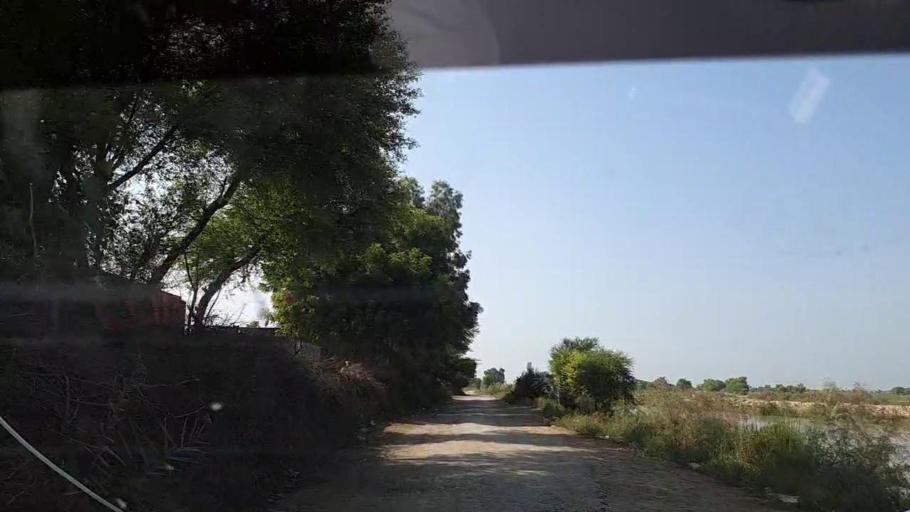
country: PK
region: Sindh
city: Ghauspur
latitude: 28.2018
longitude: 69.0397
